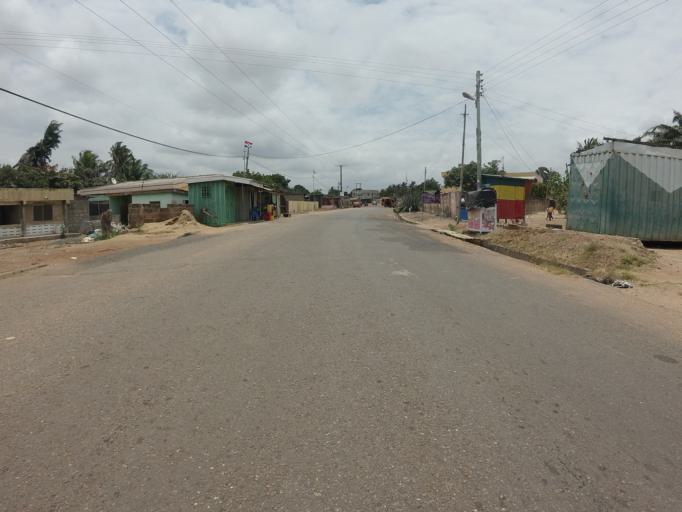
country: GH
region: Greater Accra
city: Nungua
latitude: 5.6157
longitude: -0.0787
